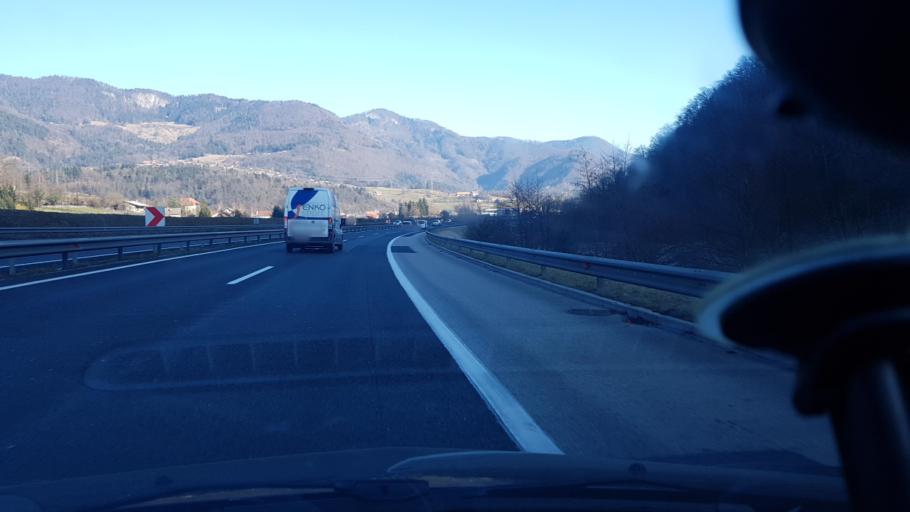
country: SI
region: Vransko
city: Vransko
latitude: 46.2357
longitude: 14.9480
